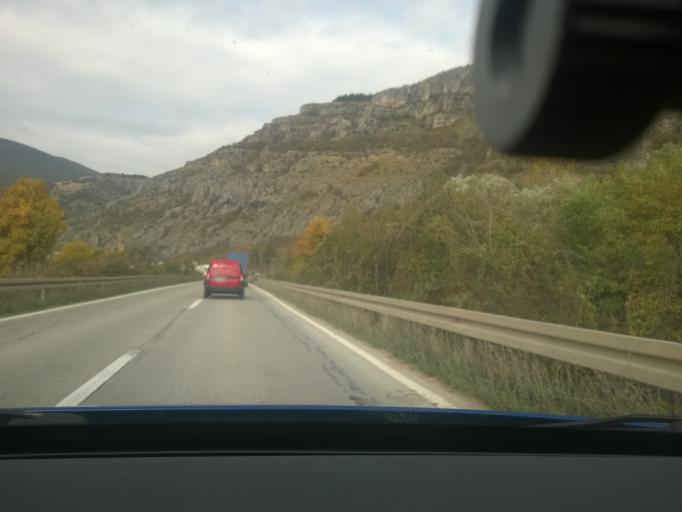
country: RS
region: Central Serbia
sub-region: Nisavski Okrug
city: Svrljig
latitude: 43.3080
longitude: 22.1874
